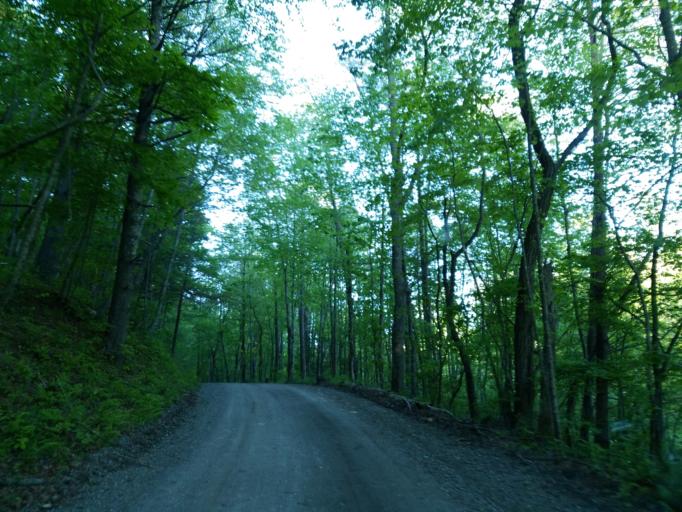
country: US
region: Georgia
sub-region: Fannin County
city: Blue Ridge
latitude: 34.7486
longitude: -84.2789
